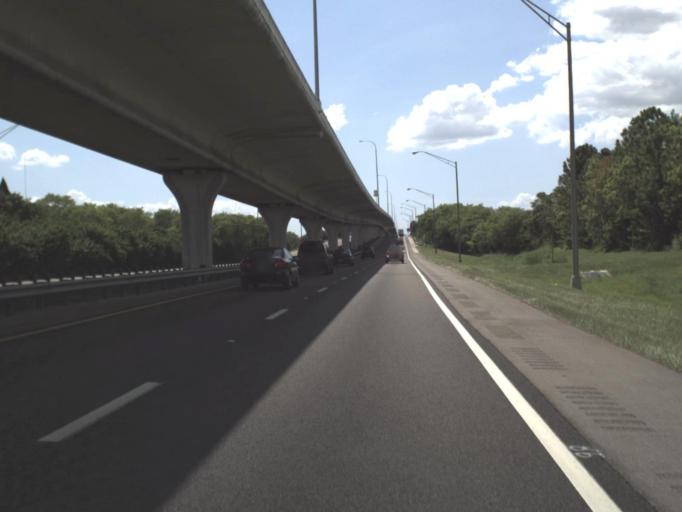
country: US
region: Florida
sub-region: Hillsborough County
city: Palm River-Clair Mel
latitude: 27.9501
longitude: -82.3907
